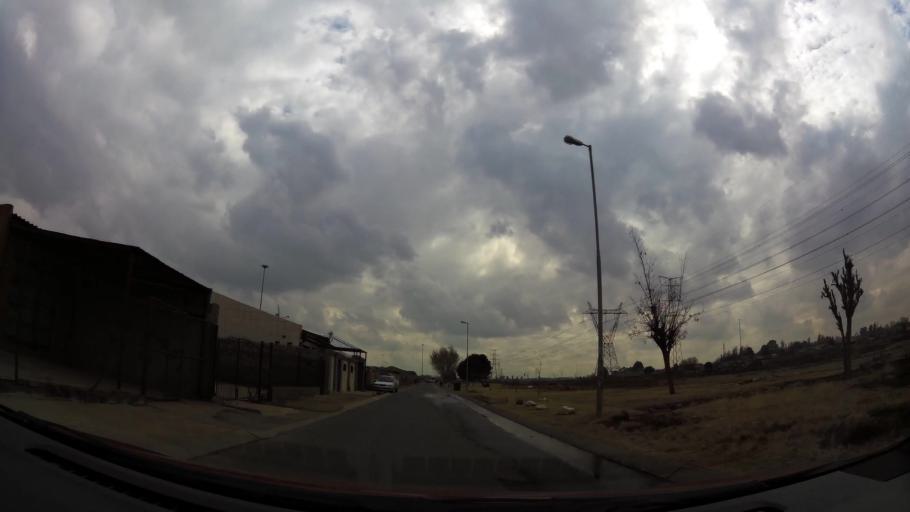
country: ZA
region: Gauteng
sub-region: City of Johannesburg Metropolitan Municipality
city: Soweto
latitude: -26.2629
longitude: 27.8386
